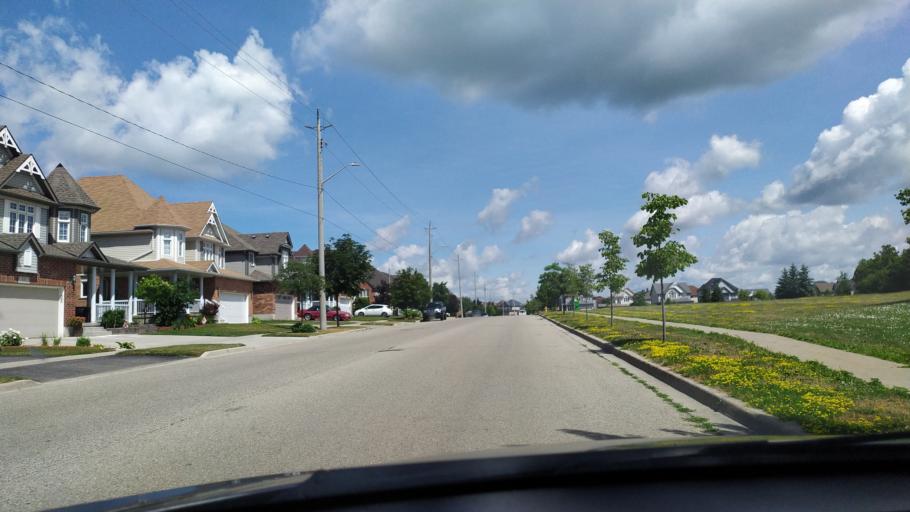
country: CA
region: Ontario
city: Kitchener
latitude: 43.4037
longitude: -80.6726
